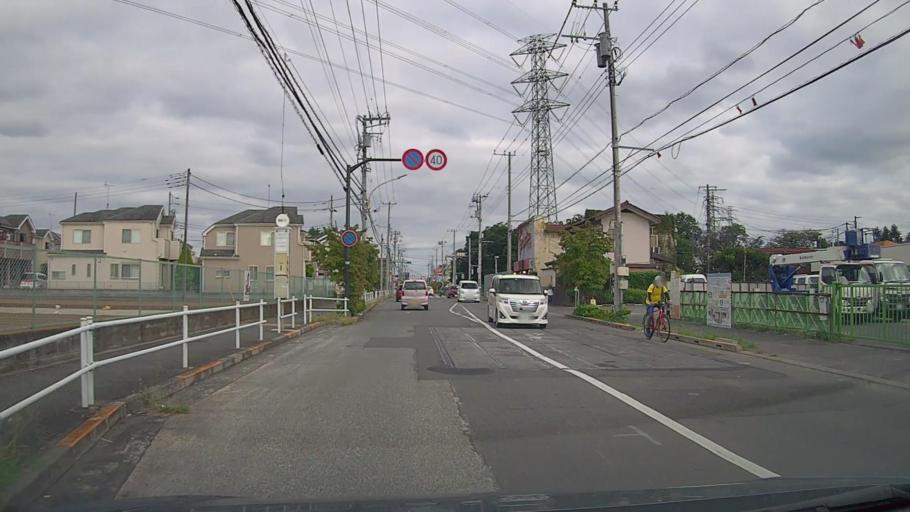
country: JP
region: Tokyo
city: Higashimurayama-shi
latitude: 35.7532
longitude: 139.5029
